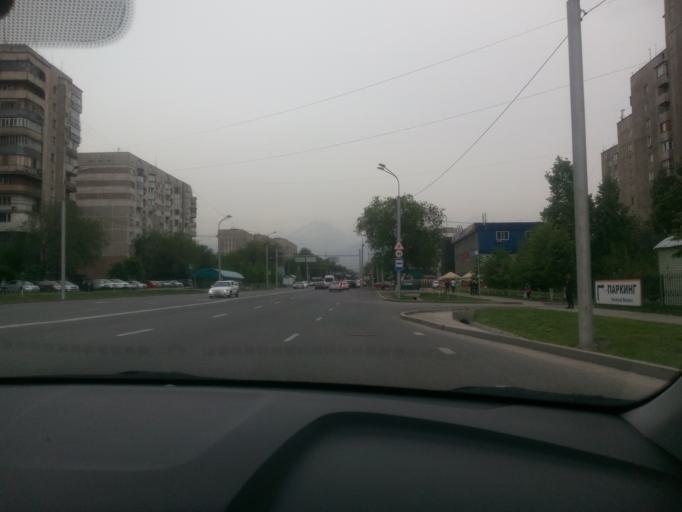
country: KZ
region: Almaty Qalasy
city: Almaty
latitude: 43.2413
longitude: 76.8285
